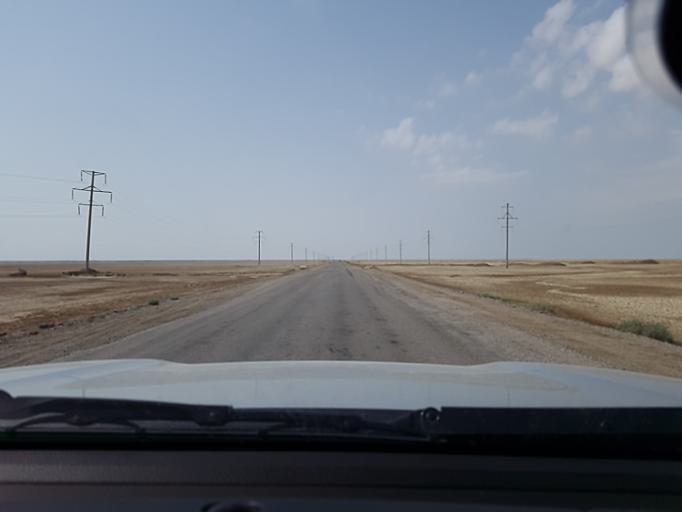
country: TM
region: Balkan
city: Gumdag
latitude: 39.0757
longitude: 54.5844
